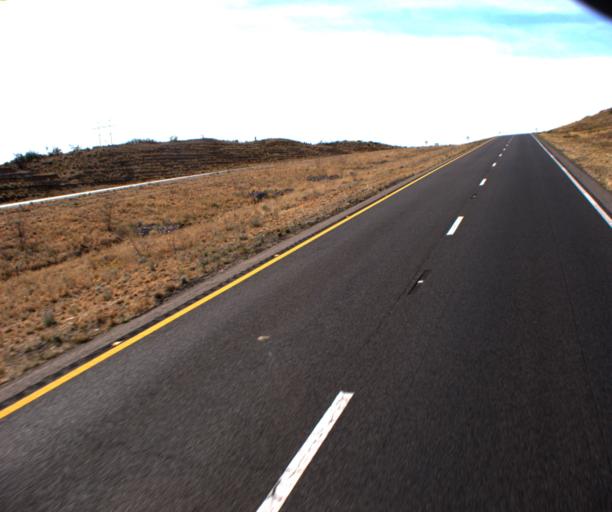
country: US
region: Arizona
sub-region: Graham County
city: Swift Trail Junction
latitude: 32.5805
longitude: -109.6826
